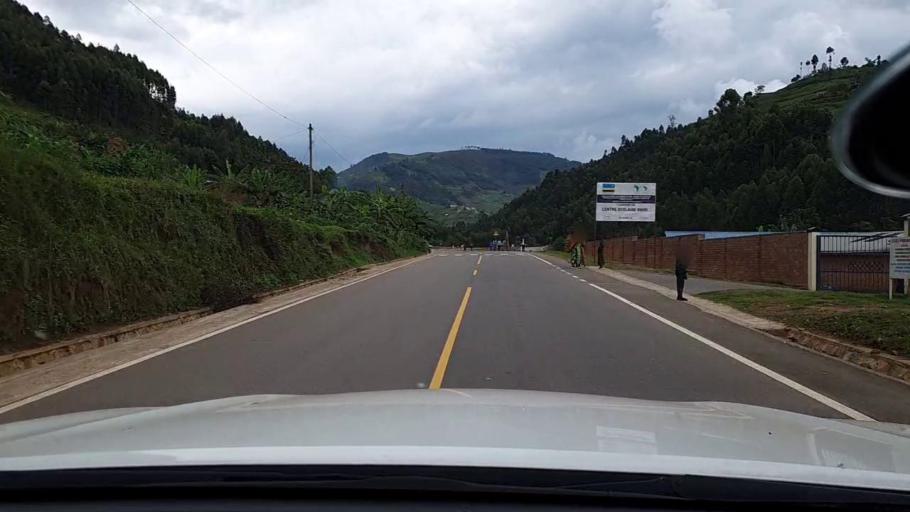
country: RW
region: Northern Province
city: Byumba
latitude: -1.6281
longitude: 29.9269
